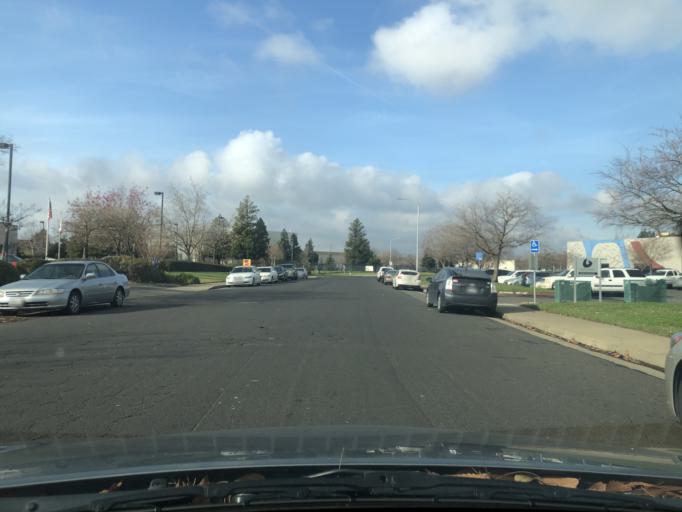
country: US
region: California
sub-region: Sacramento County
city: Rosemont
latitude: 38.5173
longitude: -121.3749
